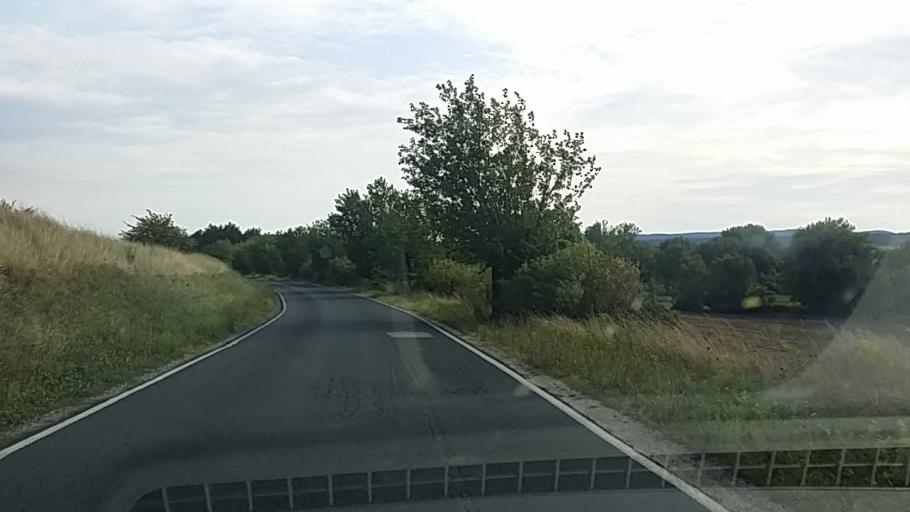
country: HU
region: Gyor-Moson-Sopron
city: Fertorakos
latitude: 47.7356
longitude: 16.6201
